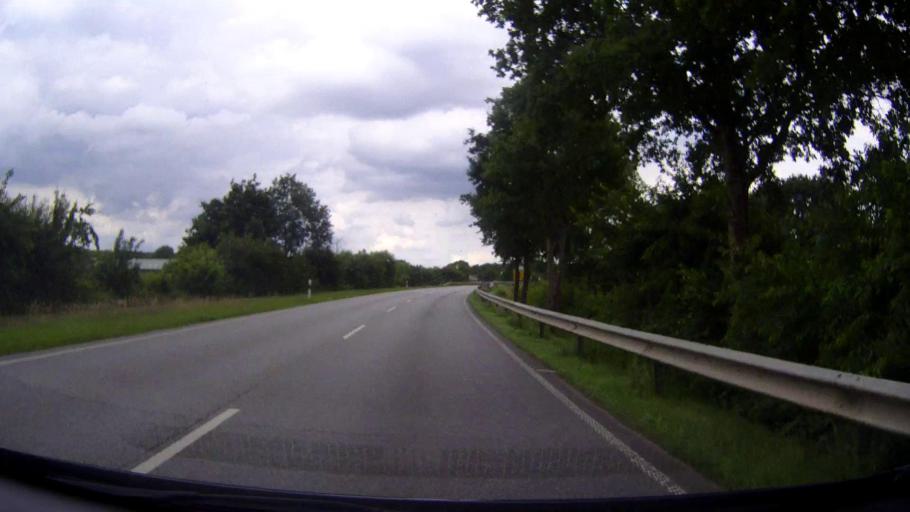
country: DE
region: Schleswig-Holstein
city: Hohenwestedt
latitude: 54.0818
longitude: 9.6560
